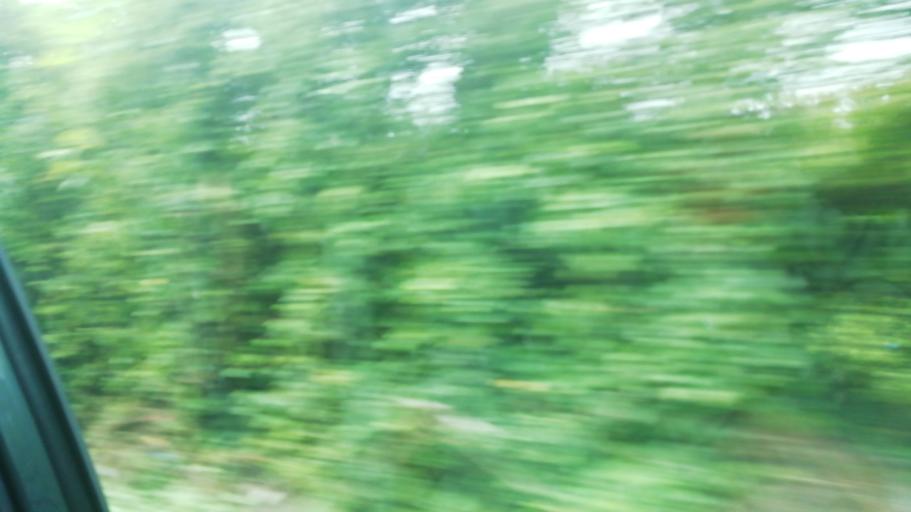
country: IE
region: Leinster
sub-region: Kilkenny
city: Callan
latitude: 52.5345
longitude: -7.5209
